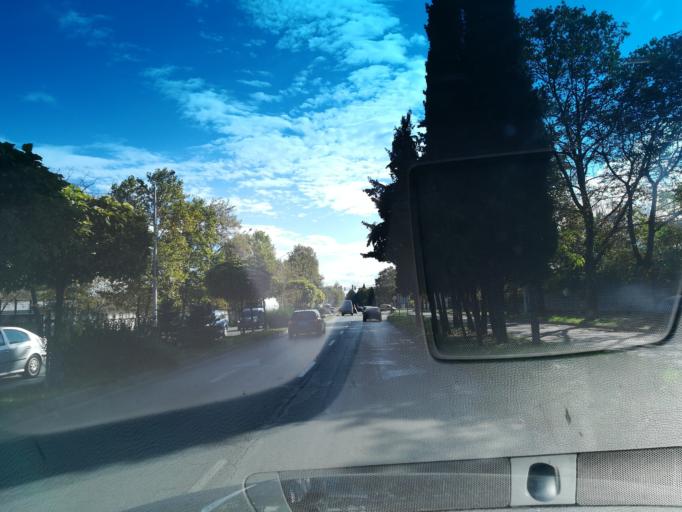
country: BG
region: Stara Zagora
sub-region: Obshtina Stara Zagora
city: Stara Zagora
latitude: 42.4110
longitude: 25.6394
